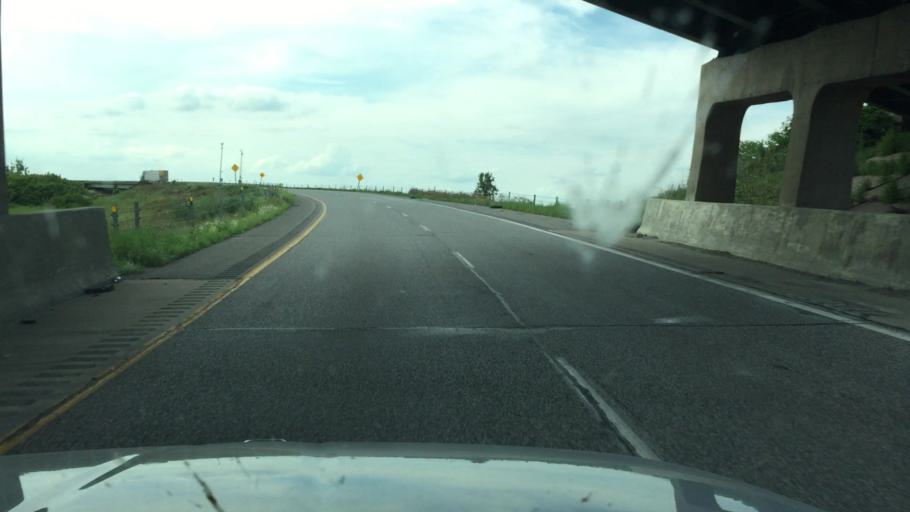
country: US
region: Iowa
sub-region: Scott County
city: Walcott
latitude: 41.6008
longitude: -90.6762
